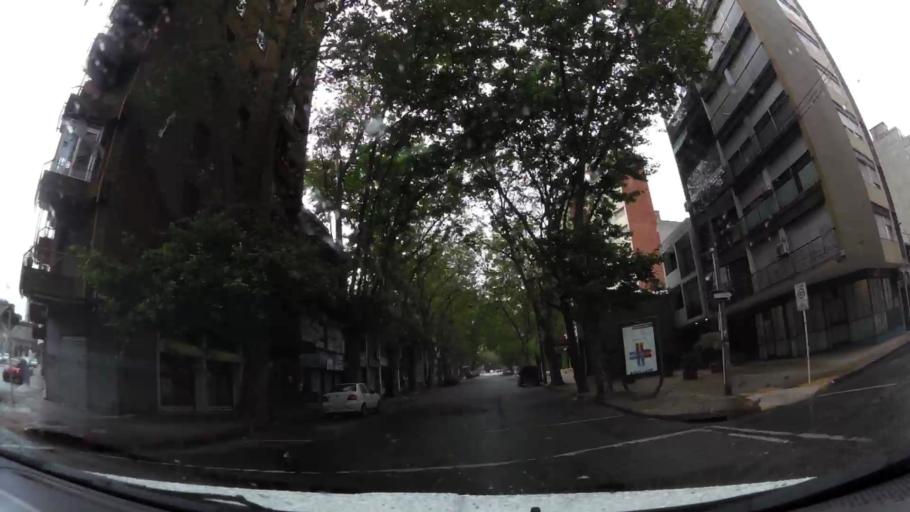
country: UY
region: Montevideo
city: Montevideo
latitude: -34.9069
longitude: -56.1762
